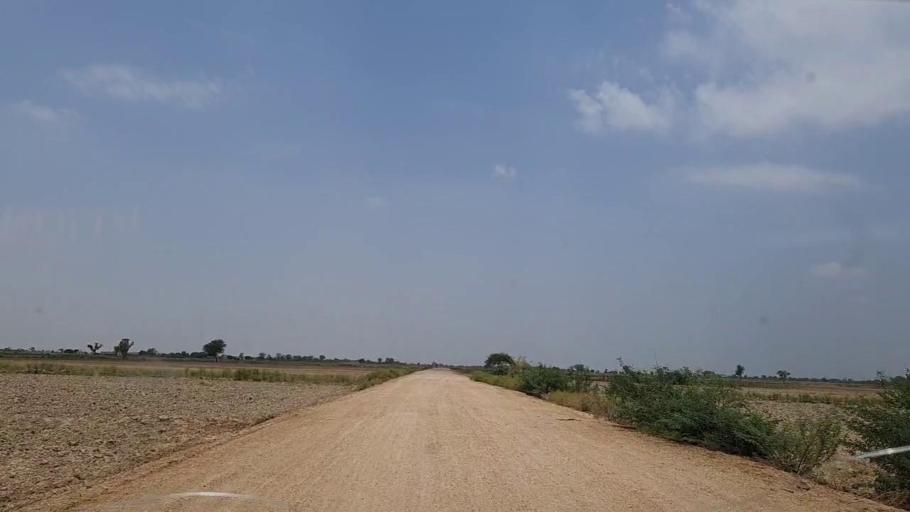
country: PK
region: Sindh
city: Phulji
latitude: 26.8071
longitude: 67.6340
